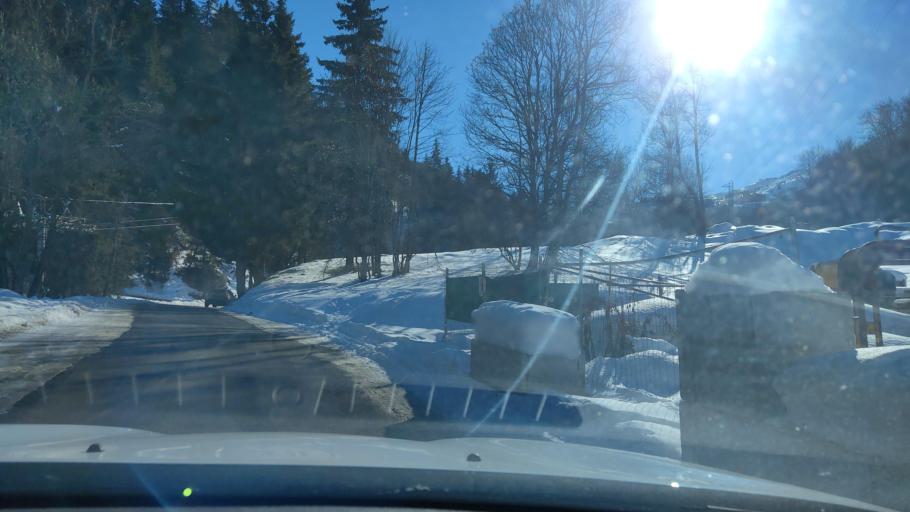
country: FR
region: Rhone-Alpes
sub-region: Departement de la Savoie
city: Les Allues
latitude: 45.4231
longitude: 6.5580
